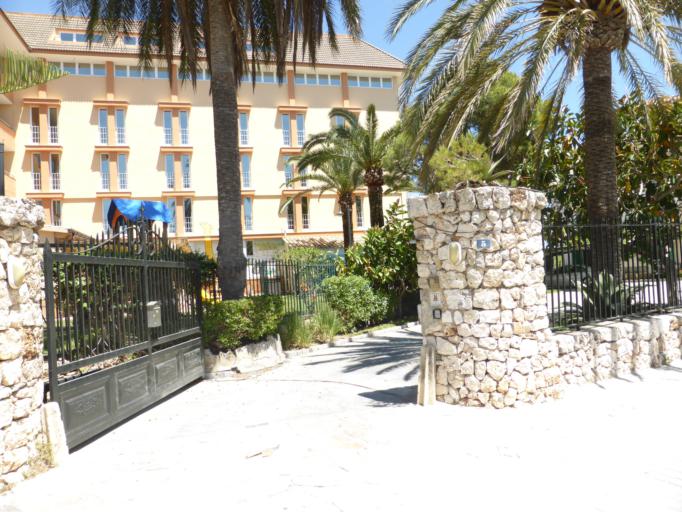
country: ES
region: Balearic Islands
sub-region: Illes Balears
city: Port d'Alcudia
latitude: 39.8302
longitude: 3.1179
